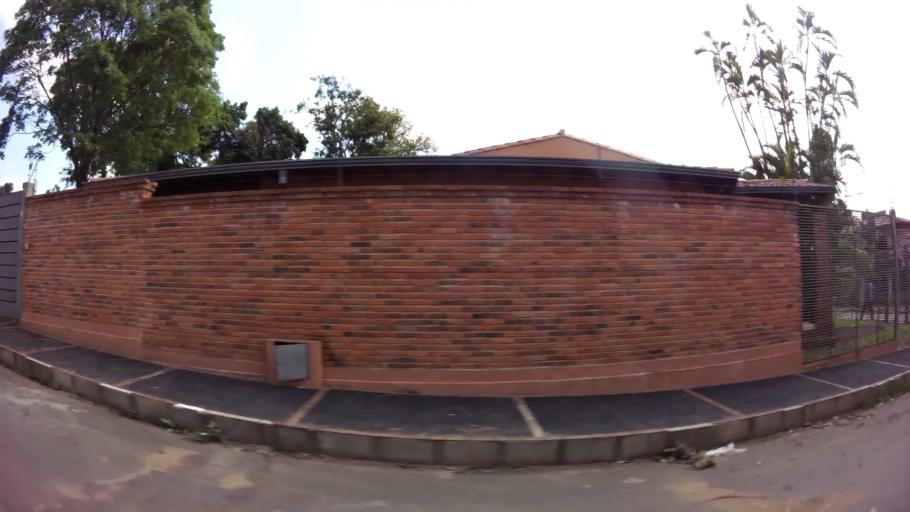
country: PY
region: Central
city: San Lorenzo
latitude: -25.3388
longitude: -57.5023
